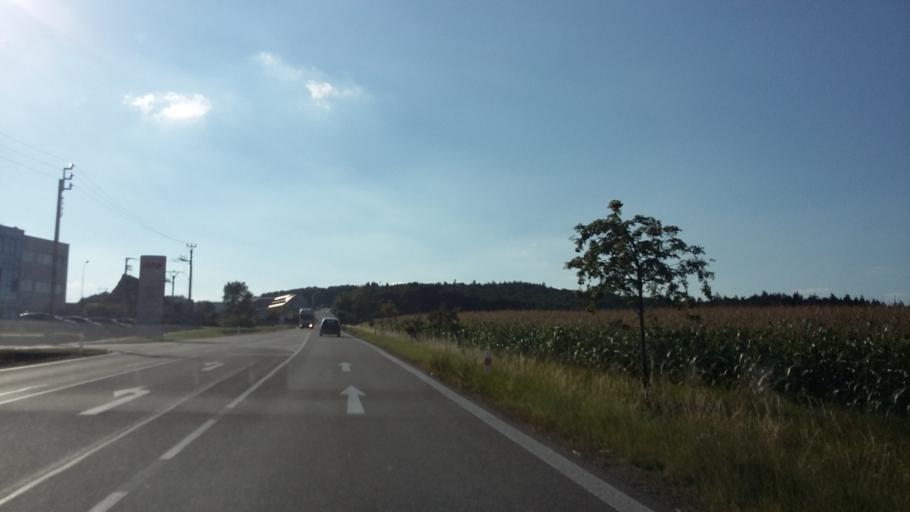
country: CZ
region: South Moravian
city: Troubsko
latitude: 49.1829
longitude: 16.4846
